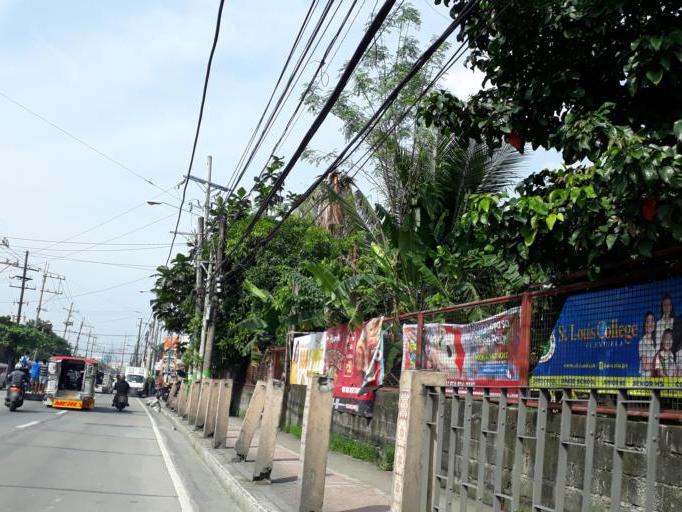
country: PH
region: Calabarzon
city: Bagong Pagasa
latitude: 14.6764
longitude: 121.0157
